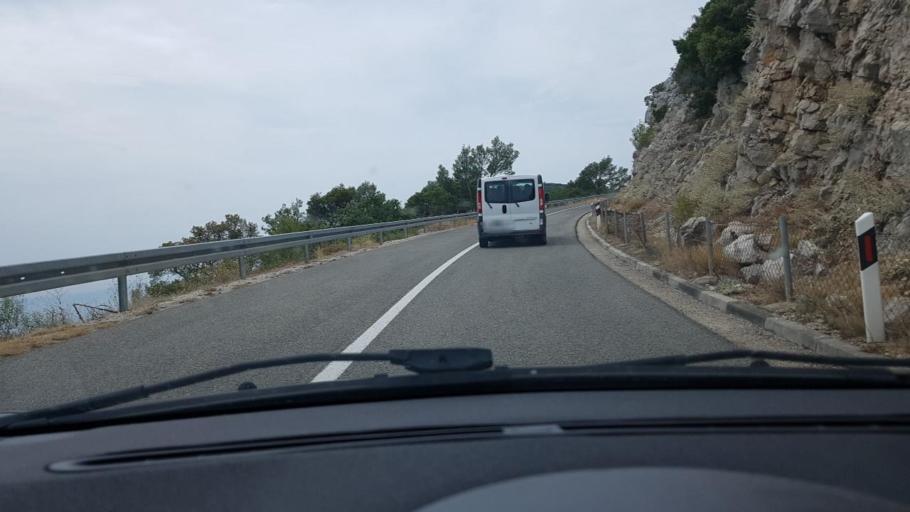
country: HR
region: Dubrovacko-Neretvanska
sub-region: Grad Korcula
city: Zrnovo
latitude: 42.9377
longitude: 17.0222
